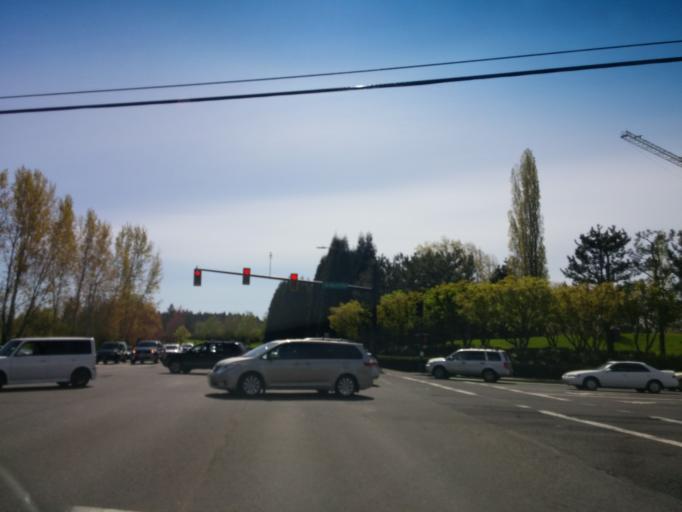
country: US
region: Oregon
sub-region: Washington County
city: Cedar Mill
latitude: 45.5108
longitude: -122.8221
